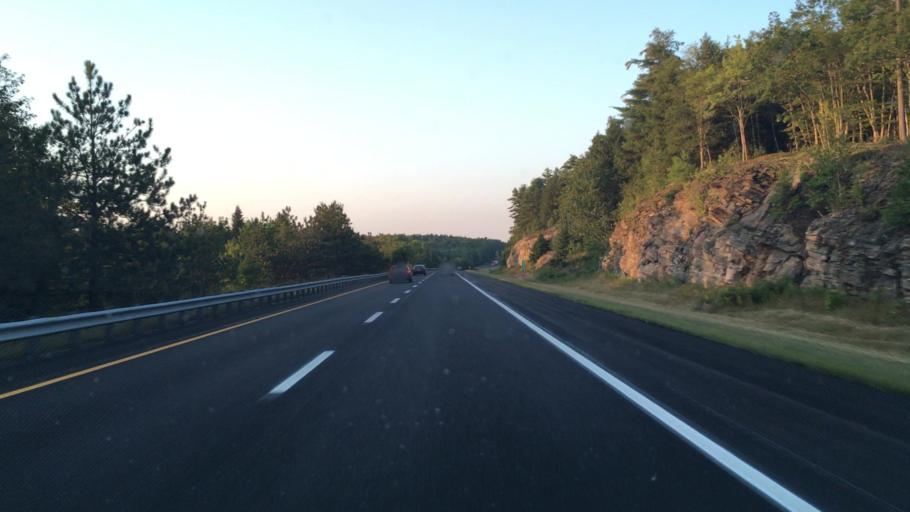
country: US
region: Maine
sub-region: Sagadahoc County
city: Topsham
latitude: 43.9761
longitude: -69.9459
